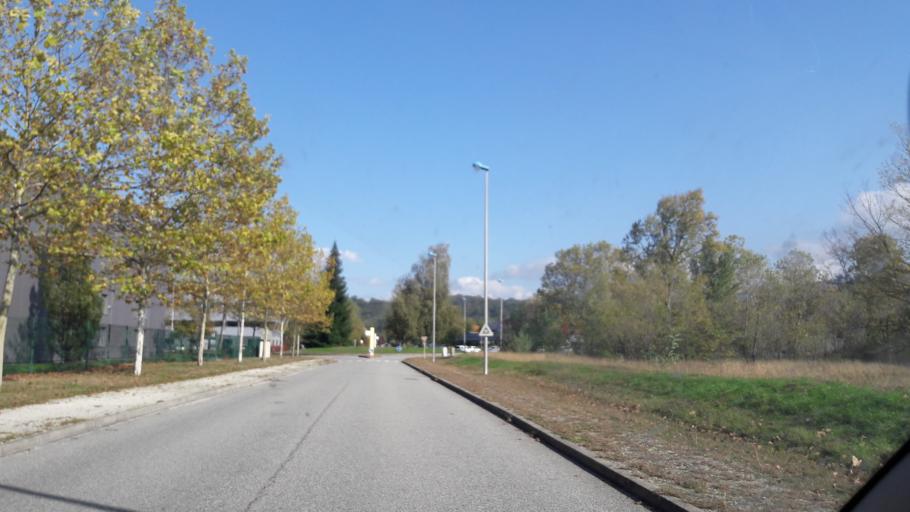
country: FR
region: Rhone-Alpes
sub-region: Departement de la Savoie
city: Montmelian
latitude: 45.4767
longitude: 6.0301
